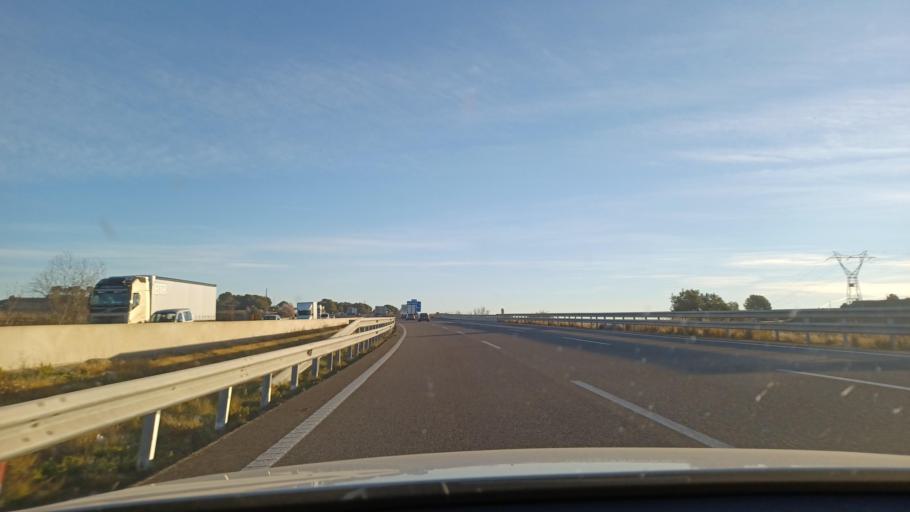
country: ES
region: Catalonia
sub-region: Provincia de Tarragona
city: Sant Jaume dels Domenys
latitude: 41.2820
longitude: 1.5747
